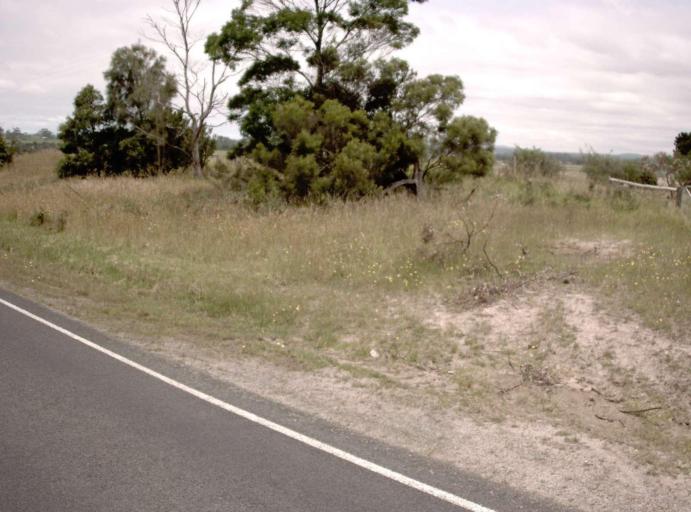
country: AU
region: Victoria
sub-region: Latrobe
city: Traralgon
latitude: -38.4991
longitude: 146.7115
